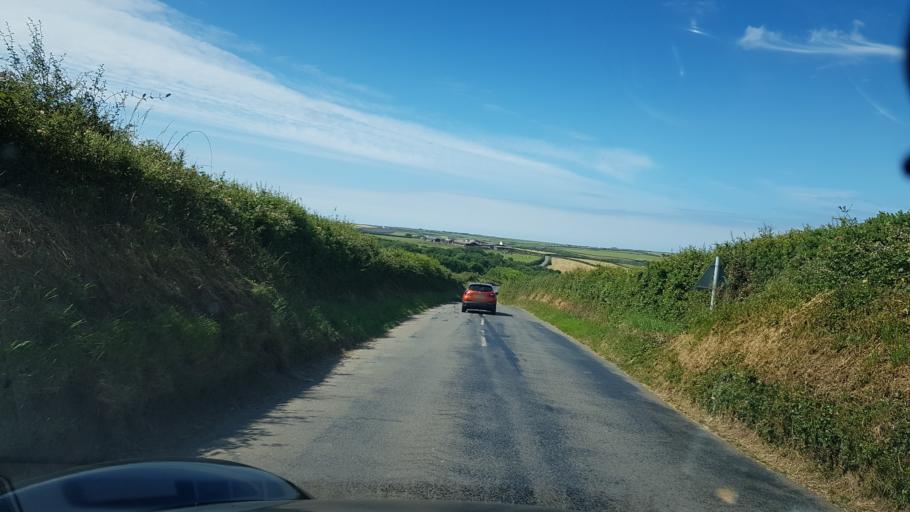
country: GB
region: Wales
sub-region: Pembrokeshire
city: Dale
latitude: 51.7411
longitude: -5.1511
